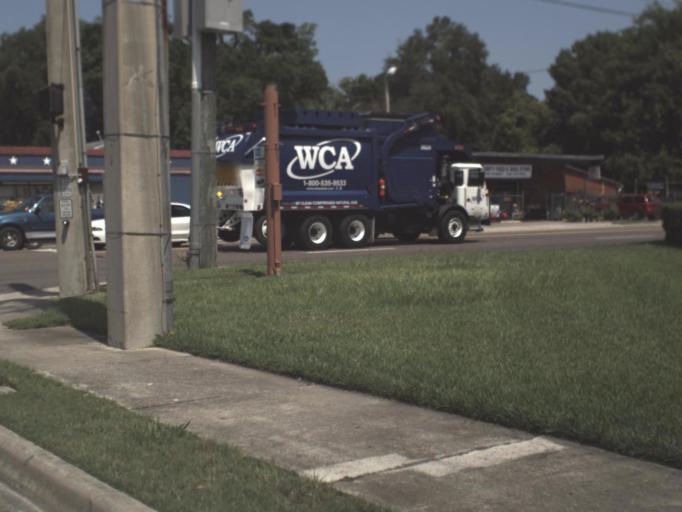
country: US
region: Florida
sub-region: Alachua County
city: Gainesville
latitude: 29.6740
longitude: -82.3305
